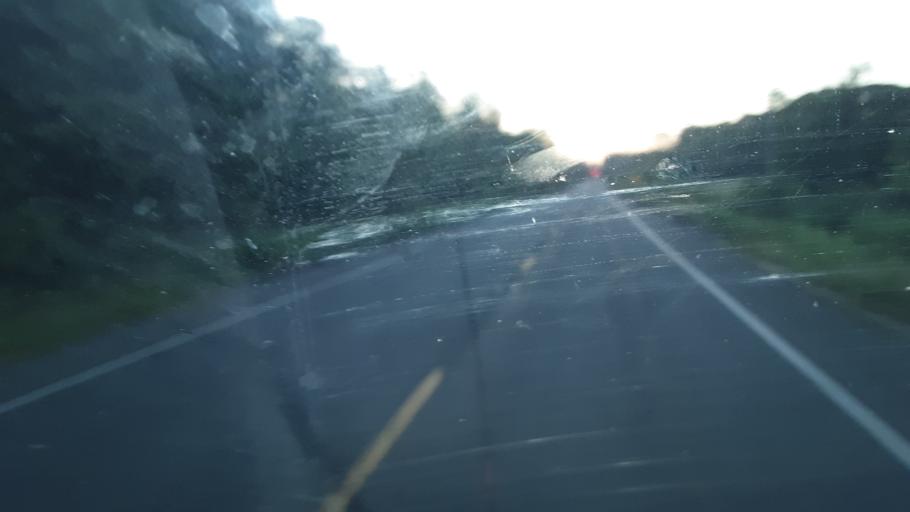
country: US
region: New York
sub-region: Saratoga County
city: Ballston Spa
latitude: 42.9961
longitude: -73.9051
